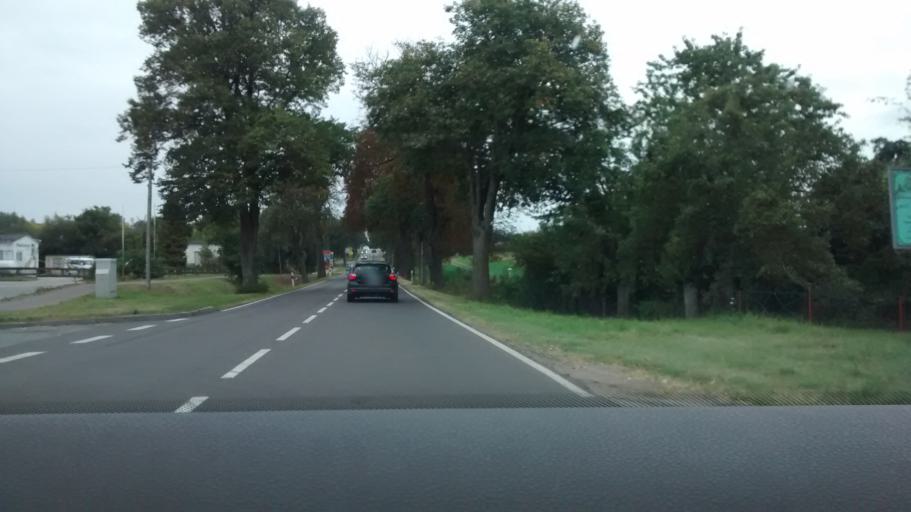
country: DE
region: Mecklenburg-Vorpommern
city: Mecklenburg
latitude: 53.8506
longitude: 11.4569
